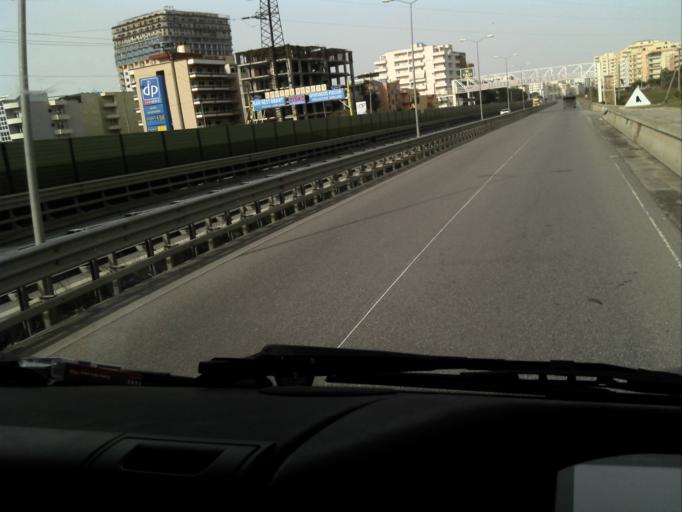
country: AL
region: Tirane
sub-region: Rrethi i Kavajes
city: Golem
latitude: 41.2670
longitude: 19.5222
